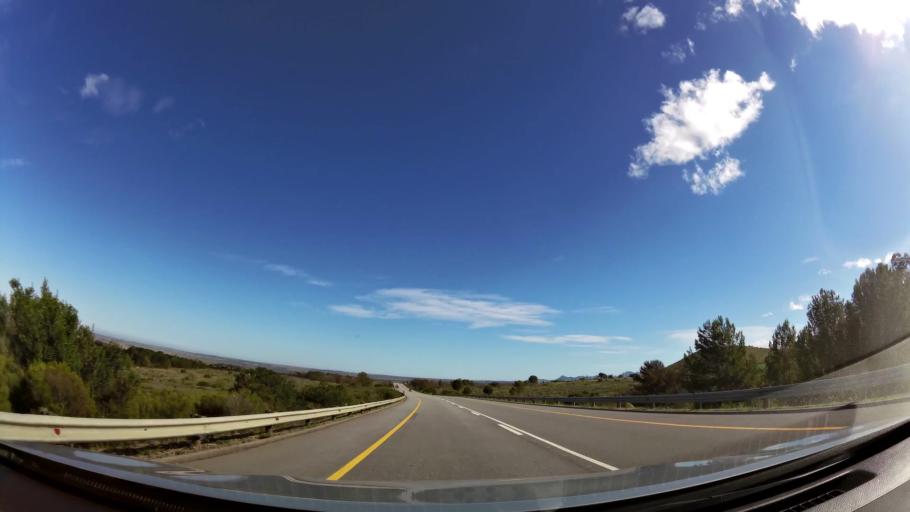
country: ZA
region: Eastern Cape
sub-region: Cacadu District Municipality
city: Kruisfontein
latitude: -33.9952
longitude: 24.6915
